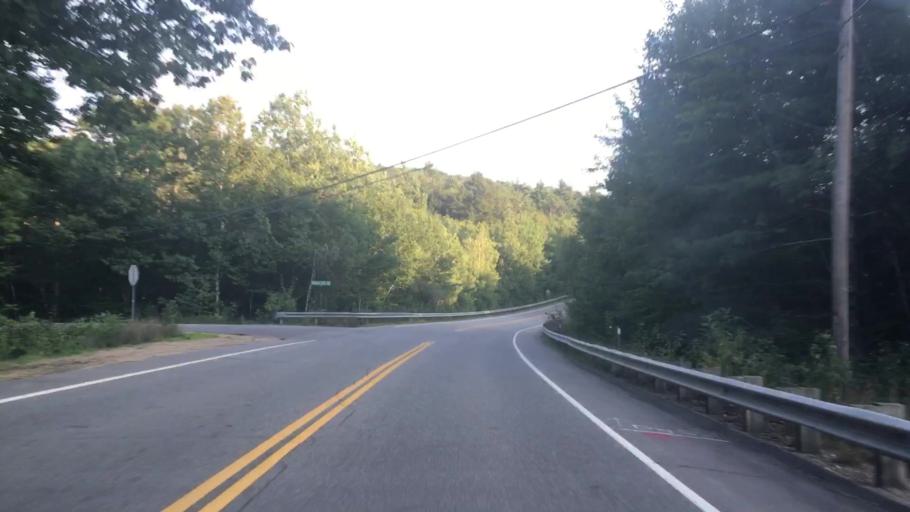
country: US
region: New Hampshire
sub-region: Belknap County
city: Gilmanton
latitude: 43.4463
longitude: -71.4193
